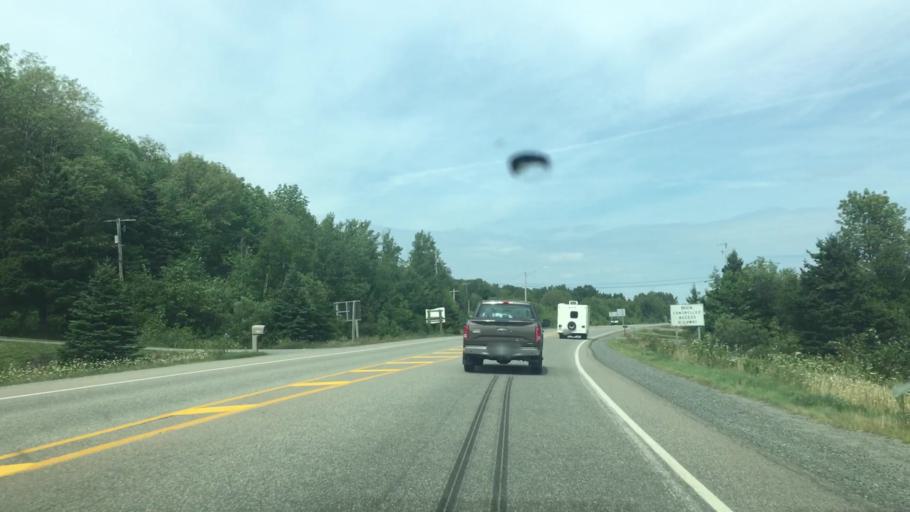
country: CA
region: Nova Scotia
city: Port Hawkesbury
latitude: 45.6565
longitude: -61.4499
